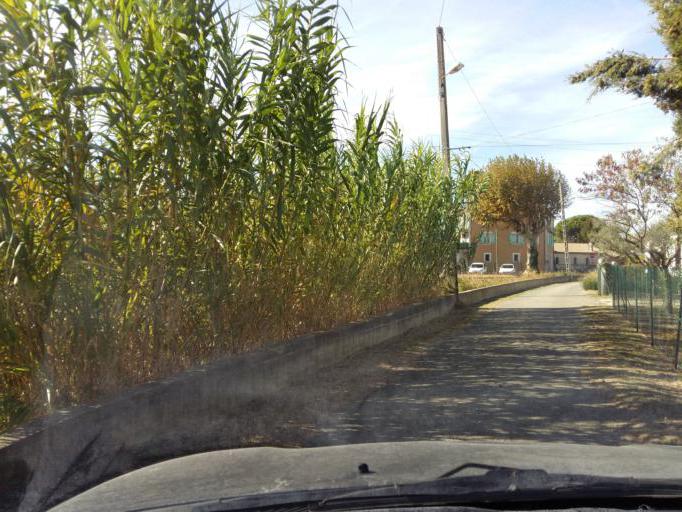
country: FR
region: Provence-Alpes-Cote d'Azur
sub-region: Departement du Vaucluse
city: Piolenc
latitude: 44.1789
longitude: 4.7645
